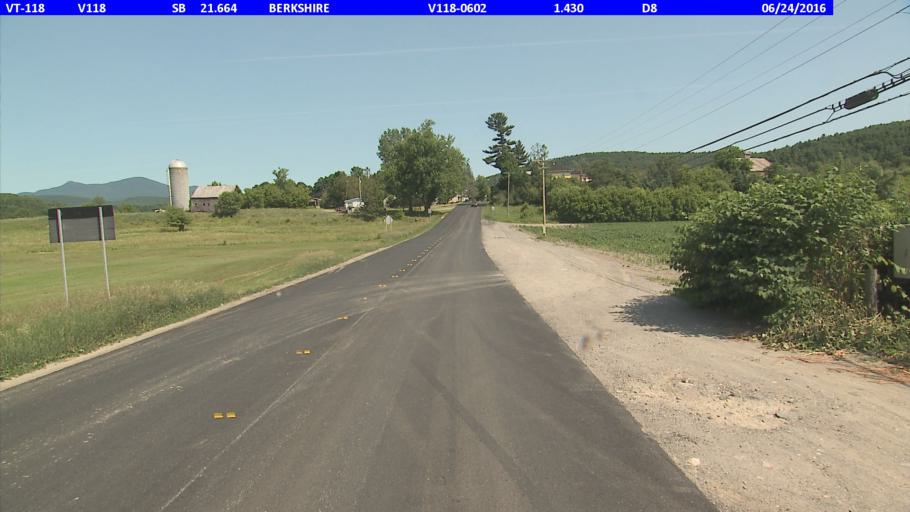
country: US
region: Vermont
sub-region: Franklin County
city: Richford
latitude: 44.9335
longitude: -72.7080
